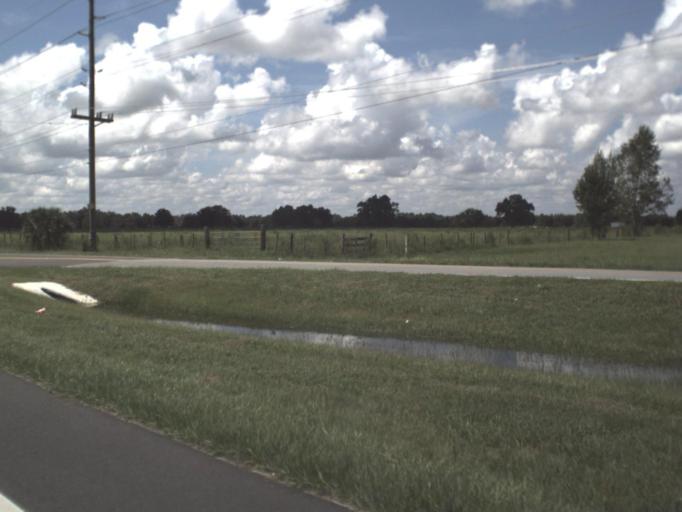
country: US
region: Florida
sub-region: Polk County
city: Polk City
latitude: 28.1678
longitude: -81.8561
